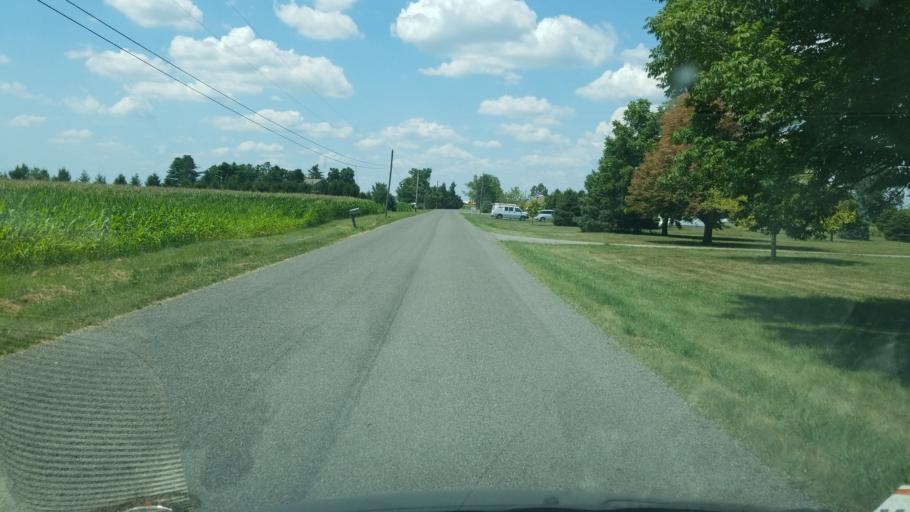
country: US
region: Ohio
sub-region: Champaign County
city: Mechanicsburg
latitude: 40.0801
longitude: -83.4568
